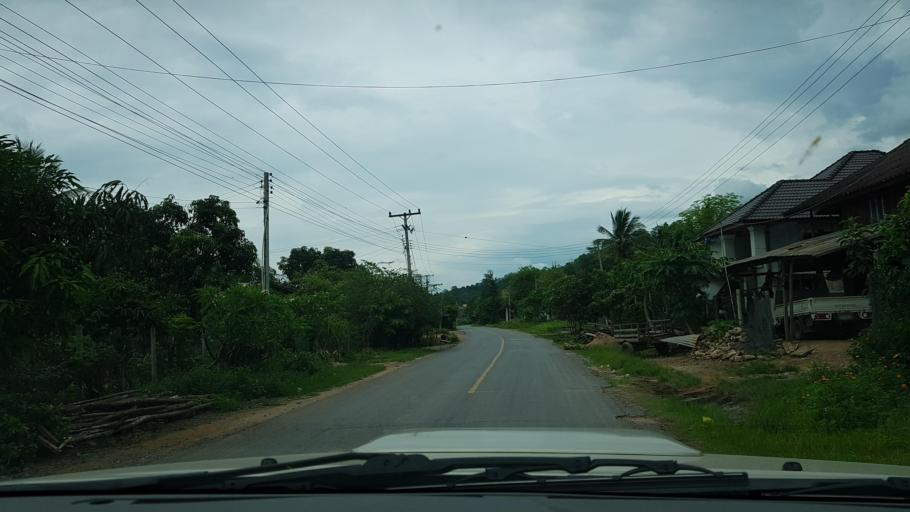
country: LA
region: Loungnamtha
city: Muang Nale
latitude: 20.3442
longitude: 101.6792
